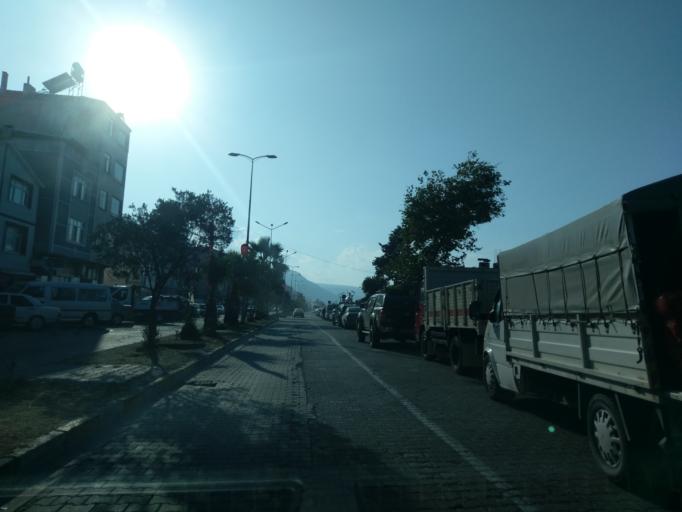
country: TR
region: Kastamonu
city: Catalzeytin
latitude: 41.9542
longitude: 34.2146
